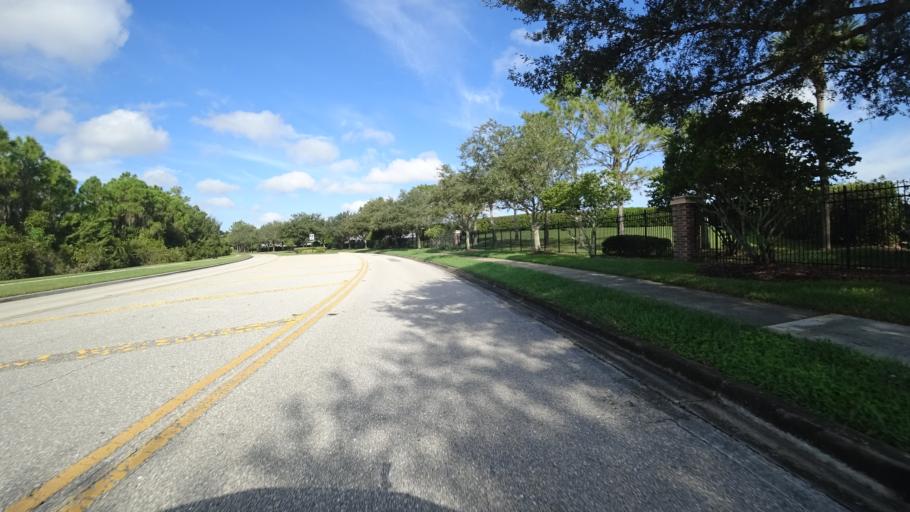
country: US
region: Florida
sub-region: Sarasota County
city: The Meadows
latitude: 27.3986
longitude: -82.4565
